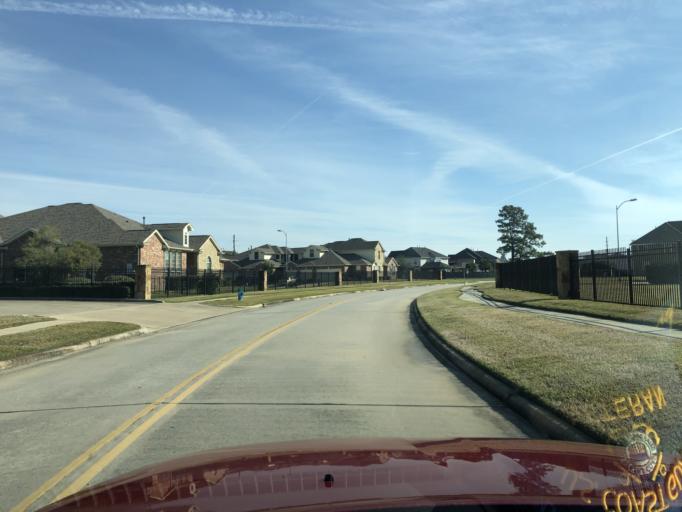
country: US
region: Texas
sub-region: Harris County
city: Tomball
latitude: 30.0383
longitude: -95.5536
